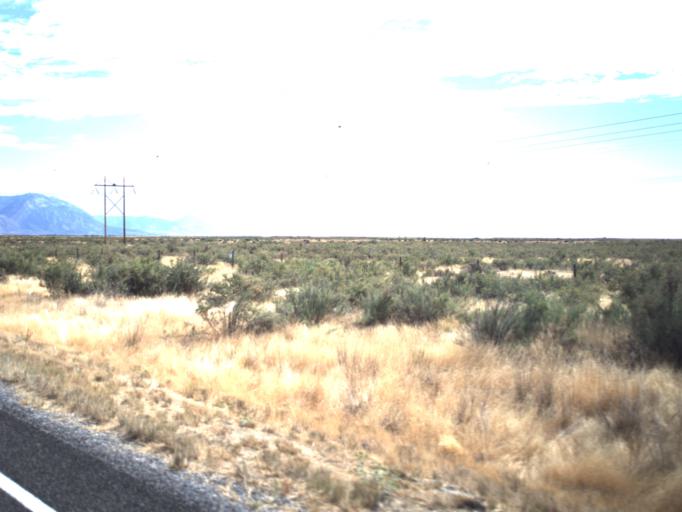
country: US
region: Utah
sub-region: Box Elder County
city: Tremonton
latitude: 41.5980
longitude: -112.2959
